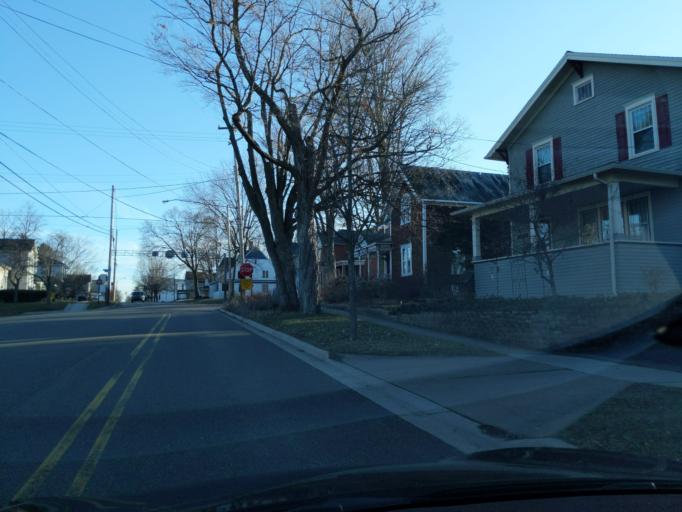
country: US
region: Michigan
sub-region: Ingham County
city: Mason
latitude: 42.5827
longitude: -84.4432
